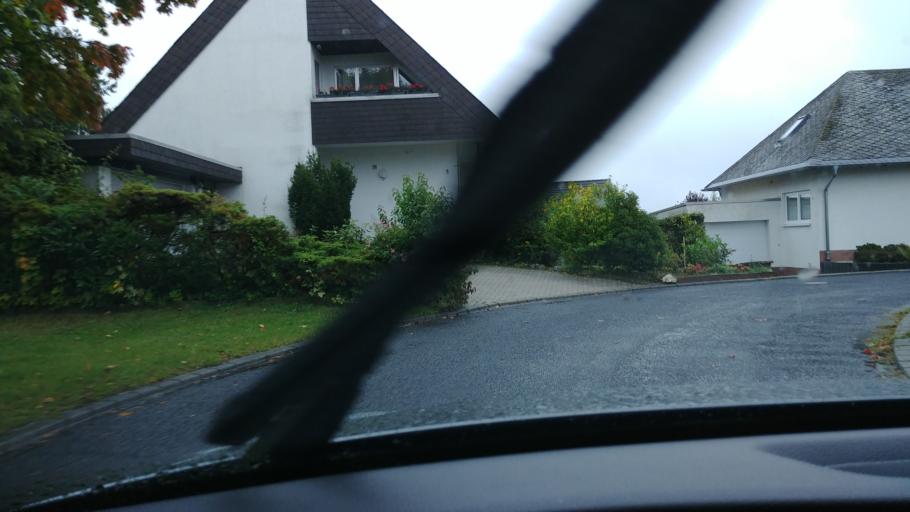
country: DE
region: Rheinland-Pfalz
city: Dohr
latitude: 50.1306
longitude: 7.1233
